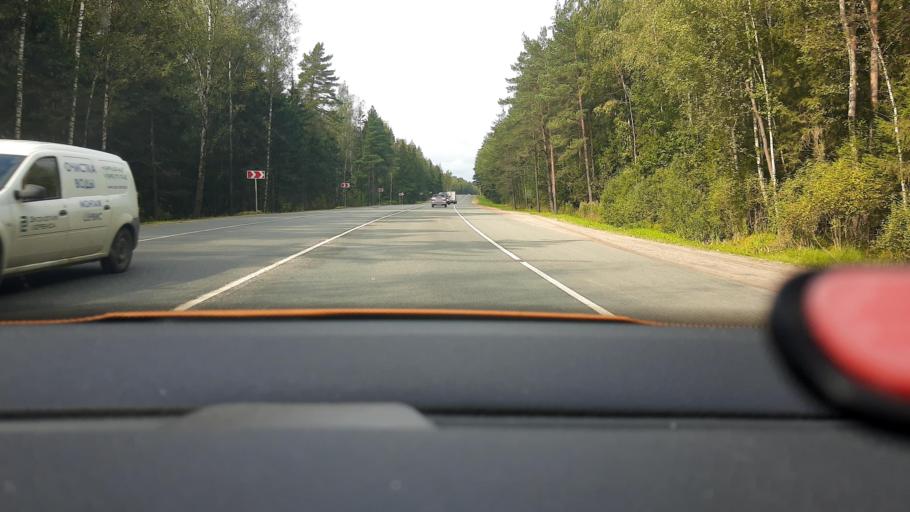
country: RU
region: Moskovskaya
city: Zelenogradskiy
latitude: 56.0843
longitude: 38.0011
